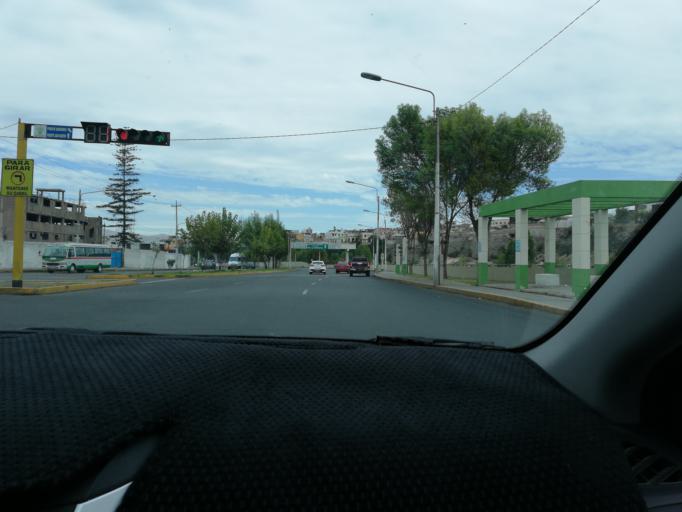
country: PE
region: Arequipa
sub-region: Provincia de Arequipa
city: Arequipa
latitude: -16.3957
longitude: -71.5397
